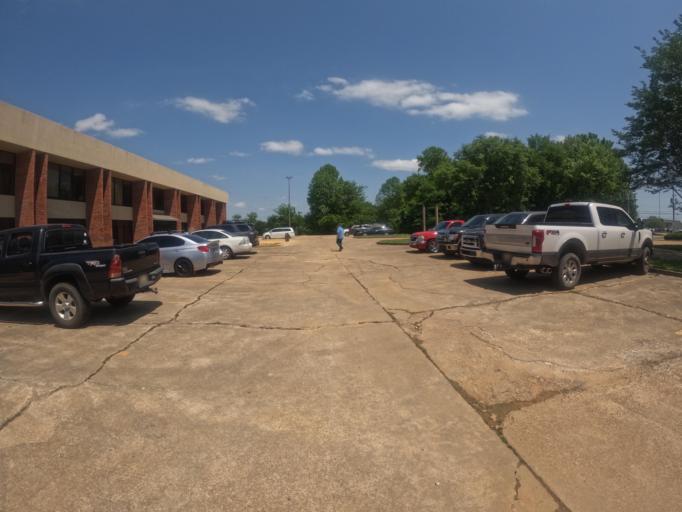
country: US
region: Mississippi
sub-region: Lee County
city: Tupelo
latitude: 34.2579
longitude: -88.7492
